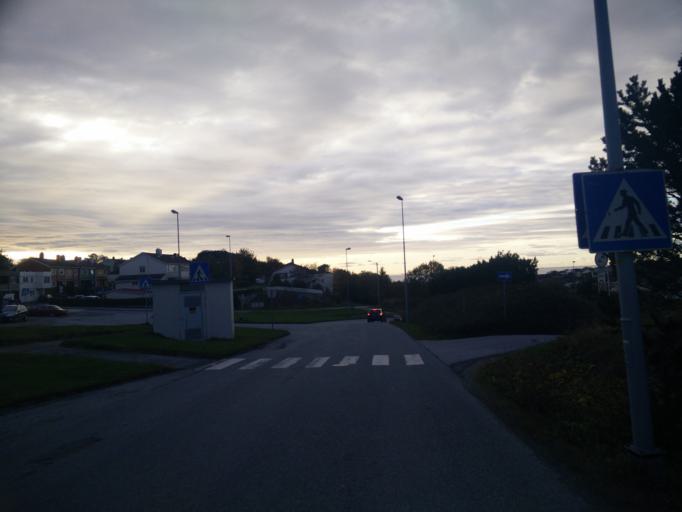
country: NO
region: More og Romsdal
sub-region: Kristiansund
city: Kristiansund
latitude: 63.1212
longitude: 7.7172
